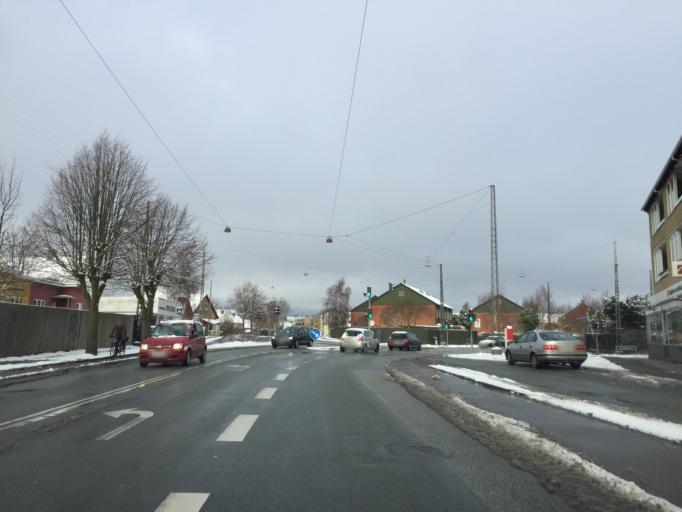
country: DK
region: Capital Region
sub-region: Tarnby Kommune
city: Tarnby
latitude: 55.6439
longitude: 12.6289
